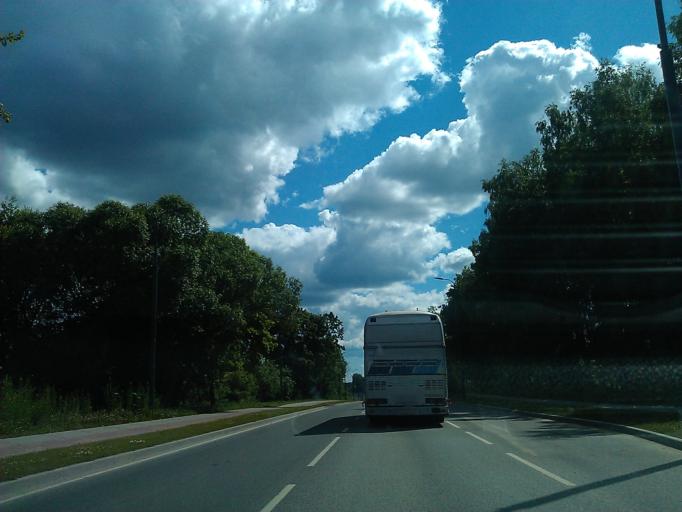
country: LV
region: Rezekne
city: Rezekne
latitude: 56.5354
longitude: 27.3485
